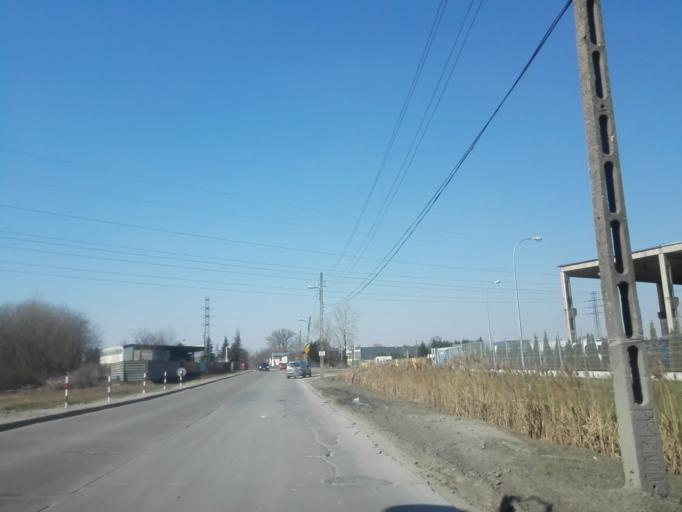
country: PL
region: Masovian Voivodeship
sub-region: Warszawa
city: Wilanow
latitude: 52.1841
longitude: 21.0831
